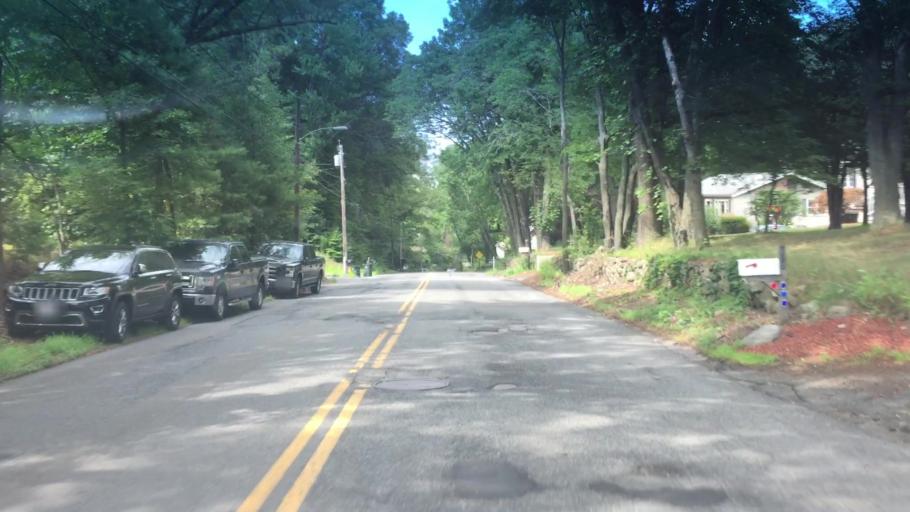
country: US
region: Massachusetts
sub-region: Norfolk County
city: Medway
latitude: 42.1362
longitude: -71.3992
